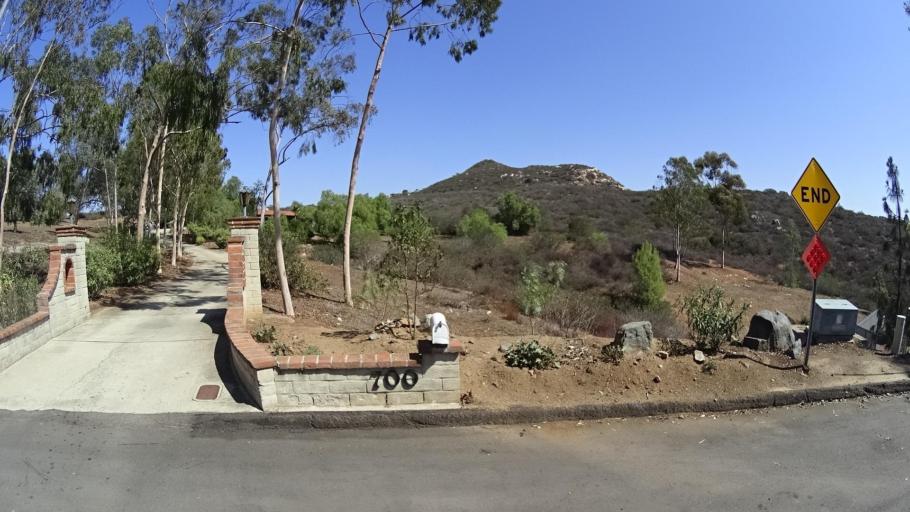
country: US
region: California
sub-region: San Diego County
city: Granite Hills
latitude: 32.8054
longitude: -116.8877
